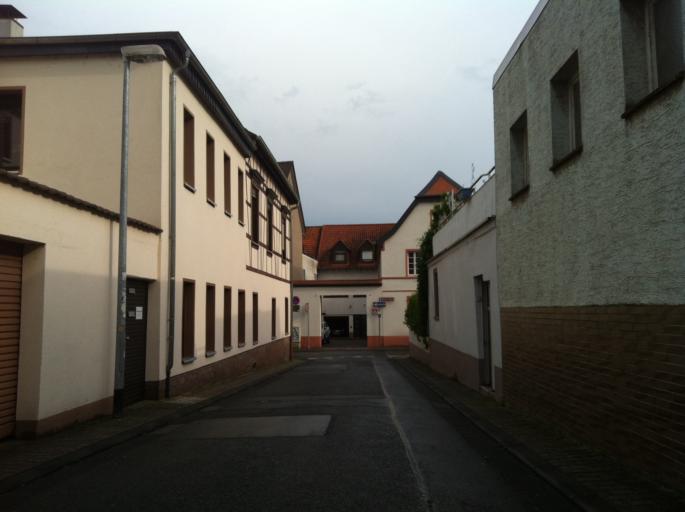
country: DE
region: Rheinland-Pfalz
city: Budenheim
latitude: 50.0004
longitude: 8.2120
